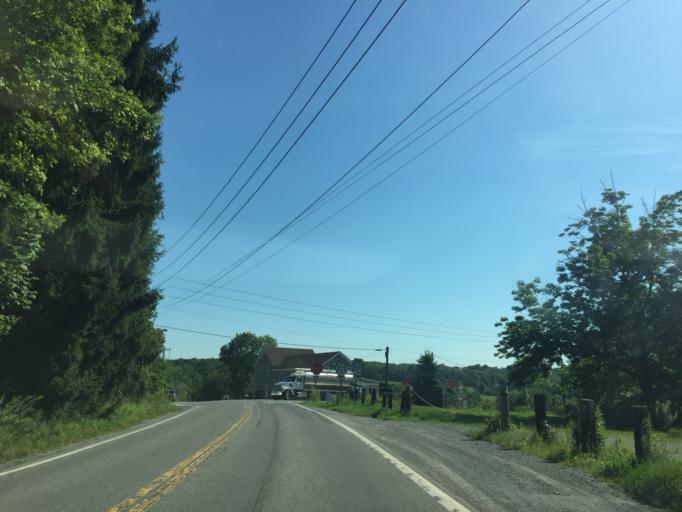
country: US
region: Pennsylvania
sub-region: Wayne County
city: Honesdale
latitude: 41.7155
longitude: -75.2299
